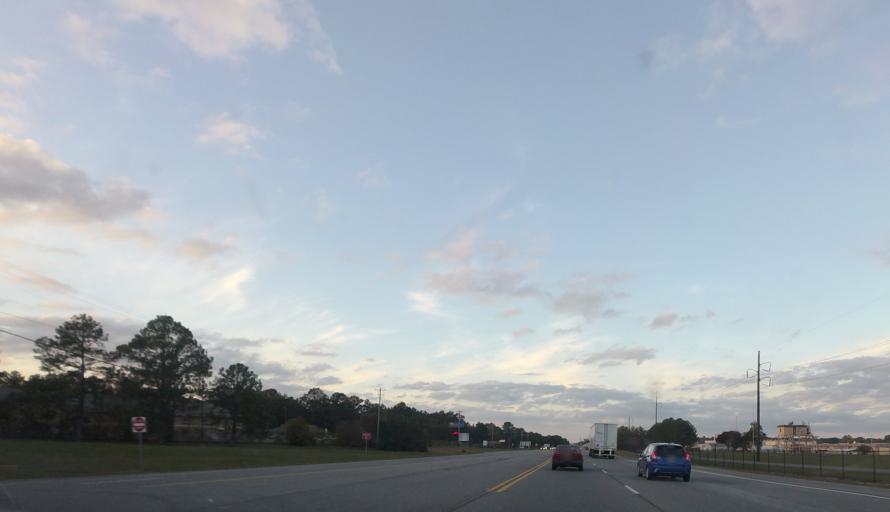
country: US
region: Georgia
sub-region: Houston County
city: Robins Air Force Base
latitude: 32.5955
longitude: -83.5916
